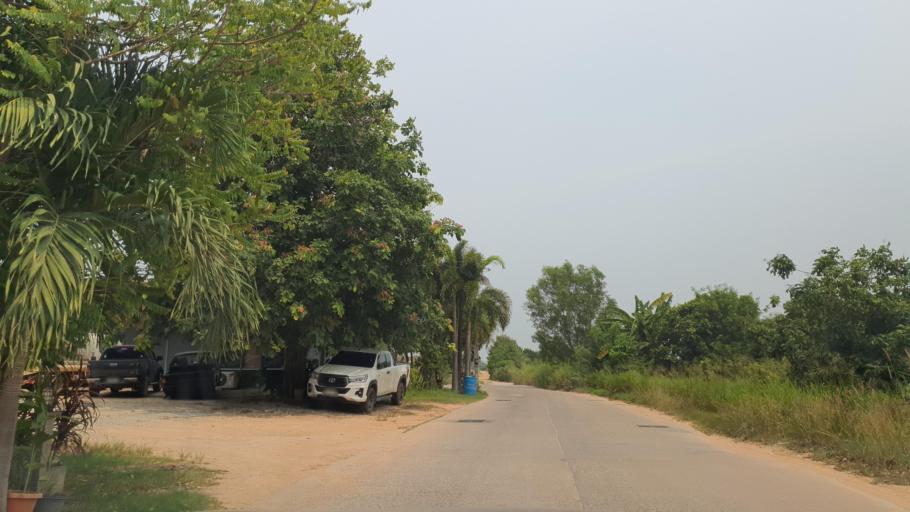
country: TH
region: Chon Buri
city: Phatthaya
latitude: 12.8857
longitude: 100.9267
